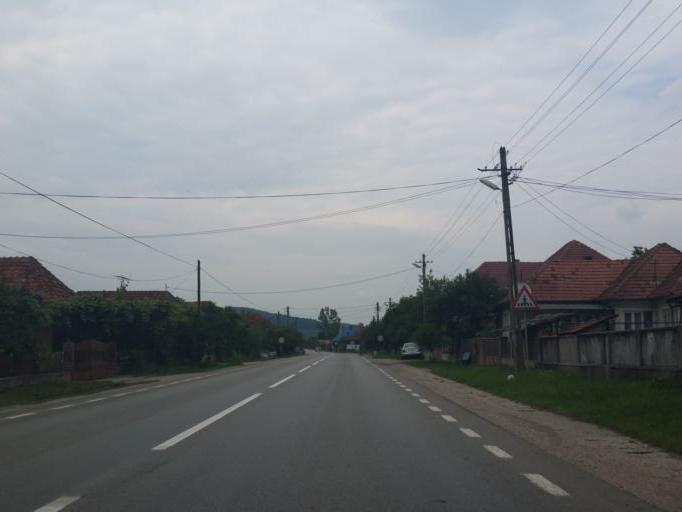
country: RO
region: Salaj
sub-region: Comuna Zimbor
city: Zimbor
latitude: 46.9863
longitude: 23.2515
